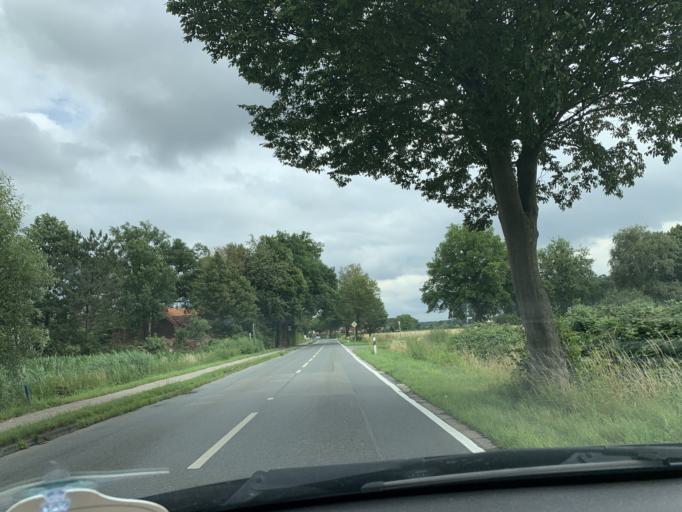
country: DE
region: North Rhine-Westphalia
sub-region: Regierungsbezirk Arnsberg
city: Lippstadt
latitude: 51.7143
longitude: 8.3106
